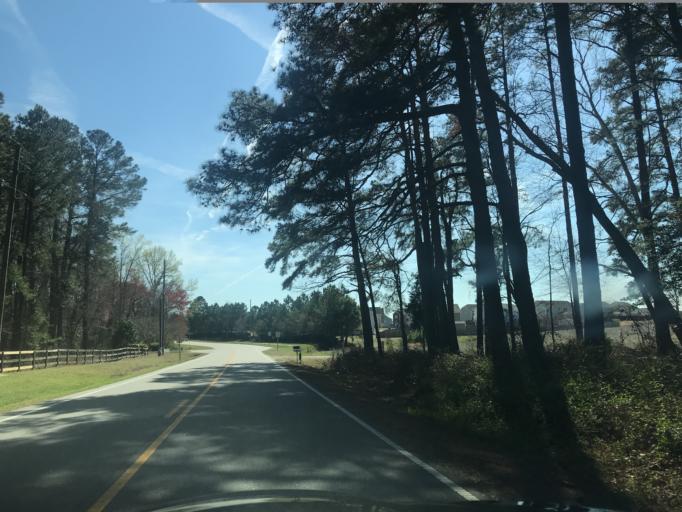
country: US
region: North Carolina
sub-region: Wake County
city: Fuquay-Varina
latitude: 35.5678
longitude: -78.7735
